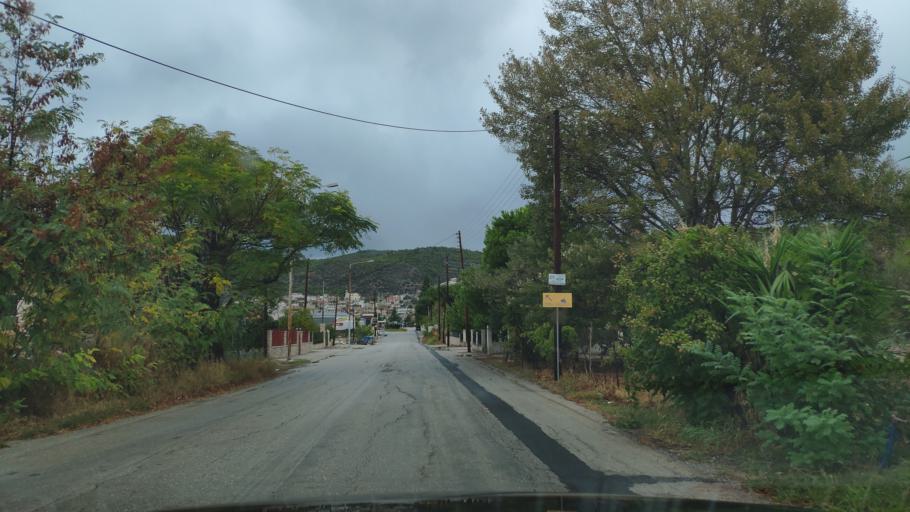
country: GR
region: Peloponnese
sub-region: Nomos Korinthias
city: Perachora
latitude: 38.0238
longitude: 22.9481
